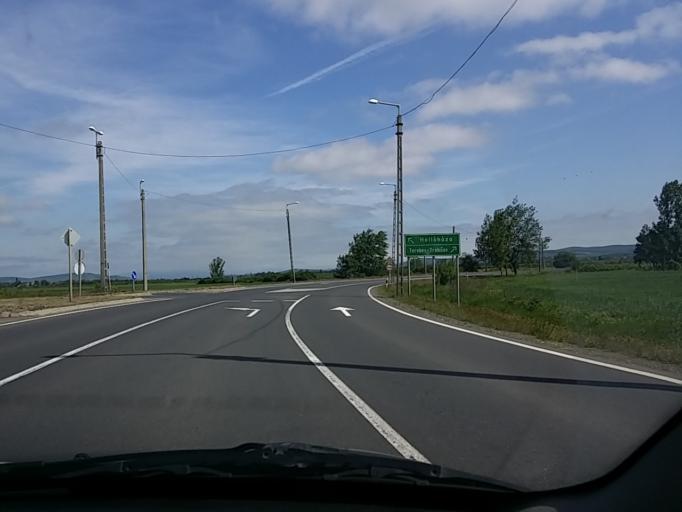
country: HU
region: Borsod-Abauj-Zemplen
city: Satoraljaujhely
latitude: 48.4184
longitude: 21.6431
